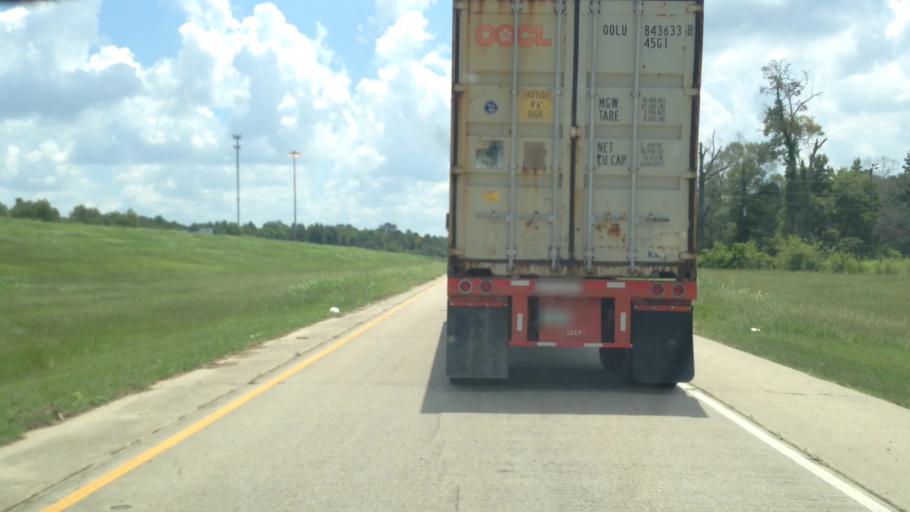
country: US
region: Louisiana
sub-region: Ascension Parish
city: Sorrento
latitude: 30.1707
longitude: -90.8766
